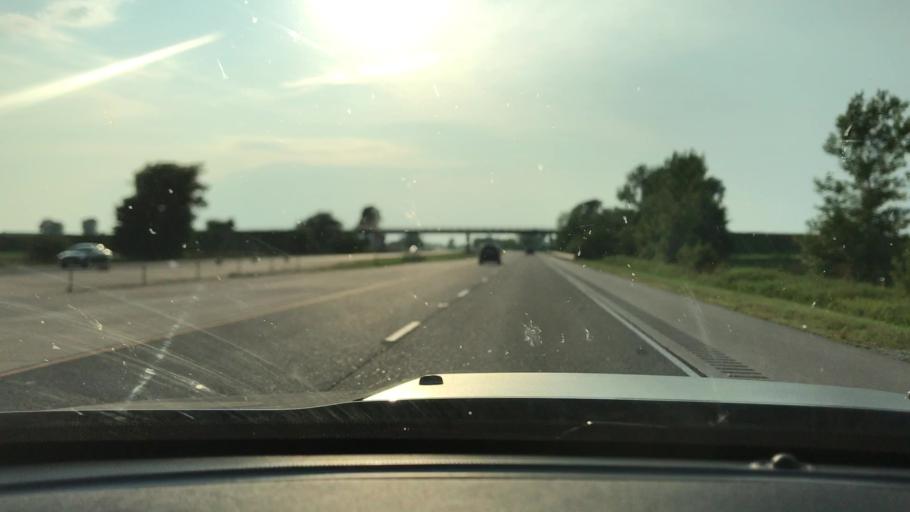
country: US
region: Illinois
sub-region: Henry County
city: Geneseo
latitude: 41.4117
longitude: -90.0273
